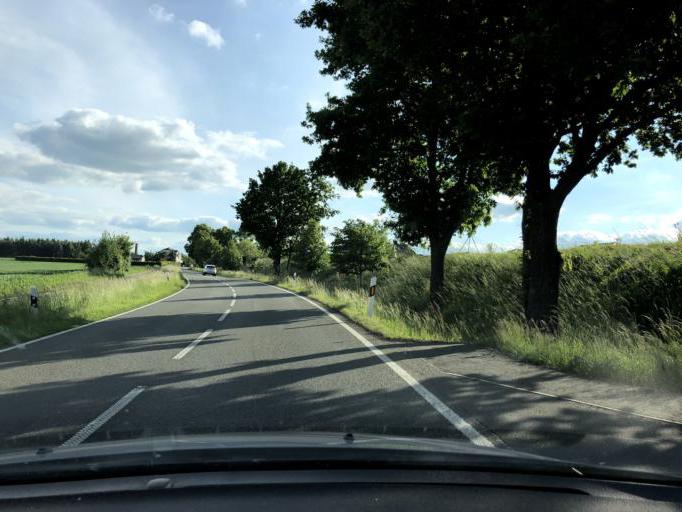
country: DE
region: Thuringia
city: Gossnitz
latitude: 50.8887
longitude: 12.4205
